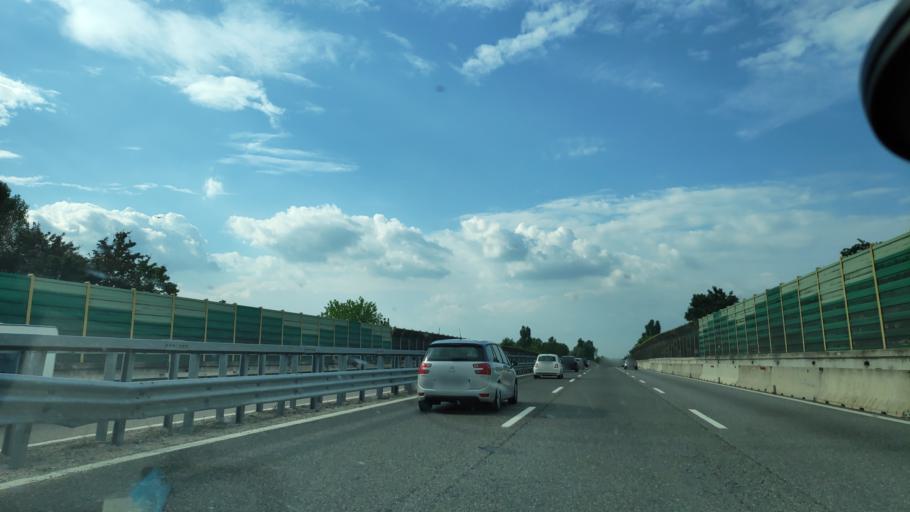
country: IT
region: Lombardy
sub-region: Provincia di Pavia
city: Zerbolo
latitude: 45.2053
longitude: 9.0175
